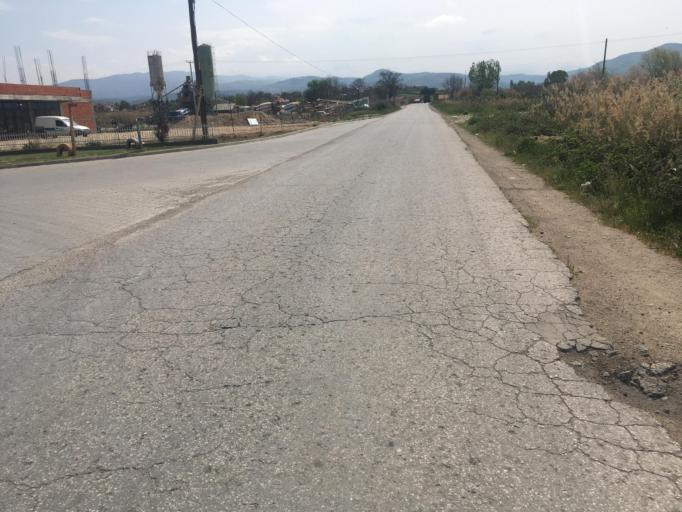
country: MK
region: Karbinci
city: Karbinci
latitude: 41.7999
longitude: 22.2193
